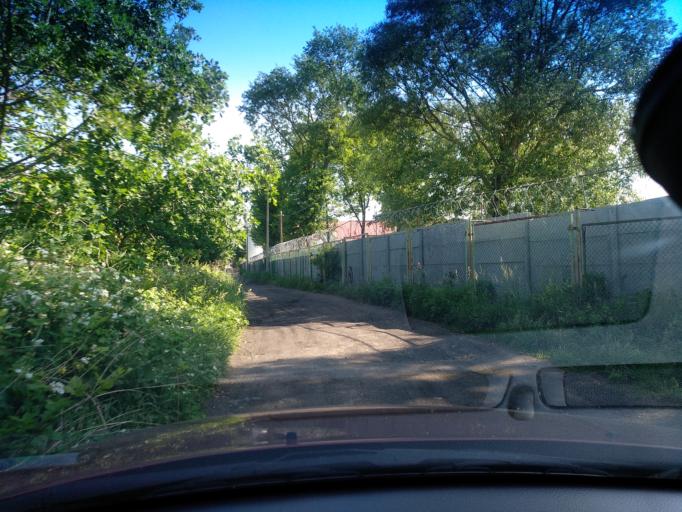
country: PL
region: Lower Silesian Voivodeship
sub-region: Powiat zgorzelecki
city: Zgorzelec
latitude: 51.1332
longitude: 15.0206
